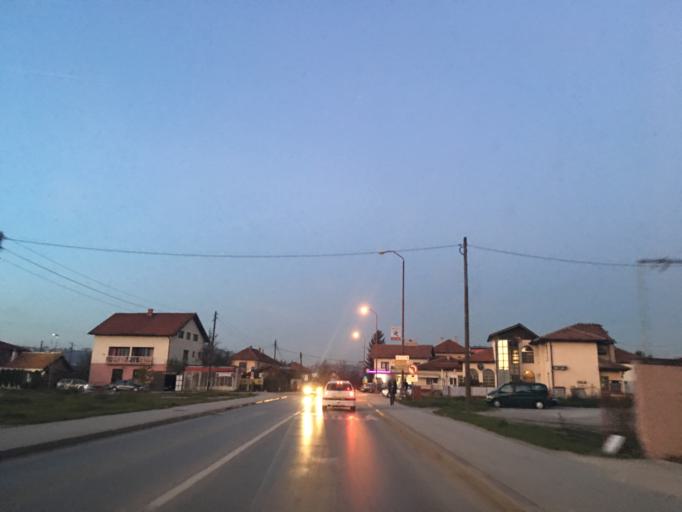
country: BA
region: Federation of Bosnia and Herzegovina
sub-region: Kanton Sarajevo
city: Sarajevo
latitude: 43.8185
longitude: 18.3562
